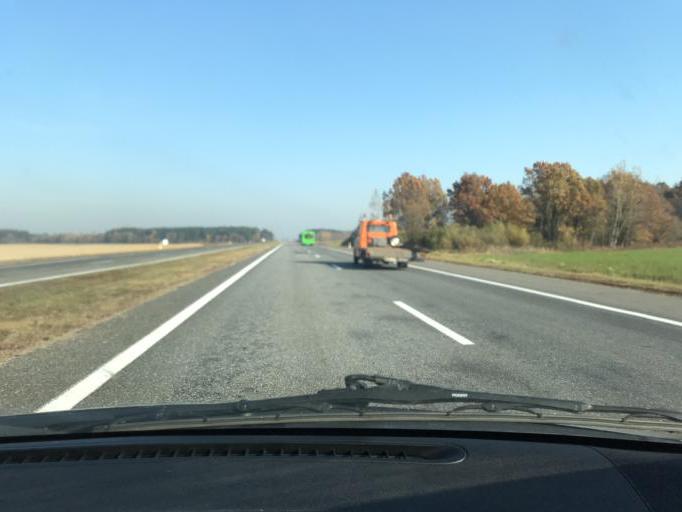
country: BY
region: Vitebsk
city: Horad Orsha
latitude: 54.5789
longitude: 30.3293
